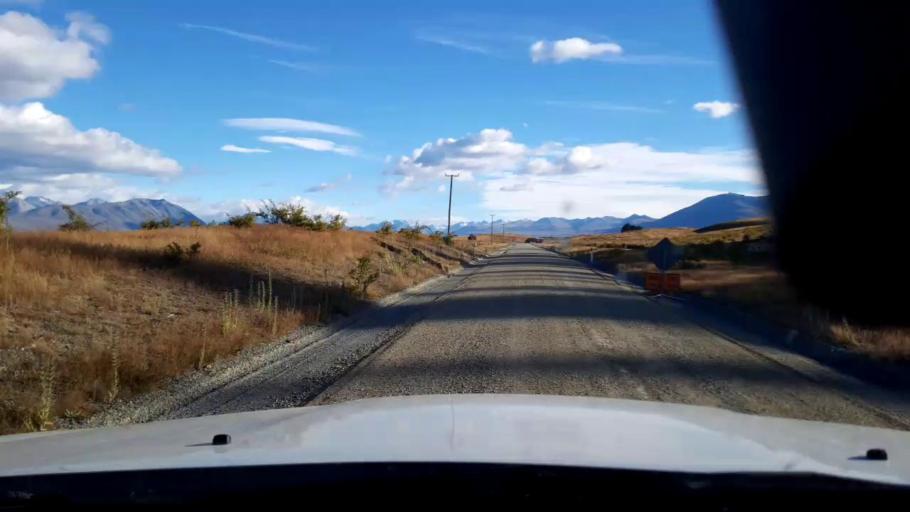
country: NZ
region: Canterbury
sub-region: Timaru District
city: Pleasant Point
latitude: -43.9808
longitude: 170.5090
